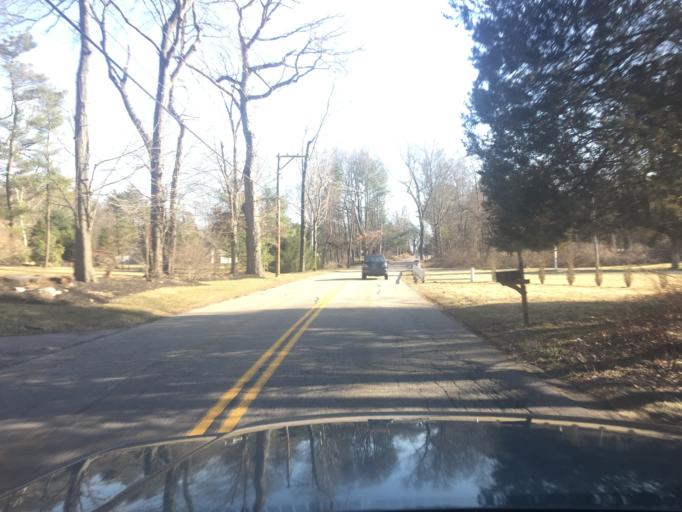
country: US
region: Massachusetts
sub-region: Norfolk County
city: Norfolk
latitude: 42.1204
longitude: -71.3593
